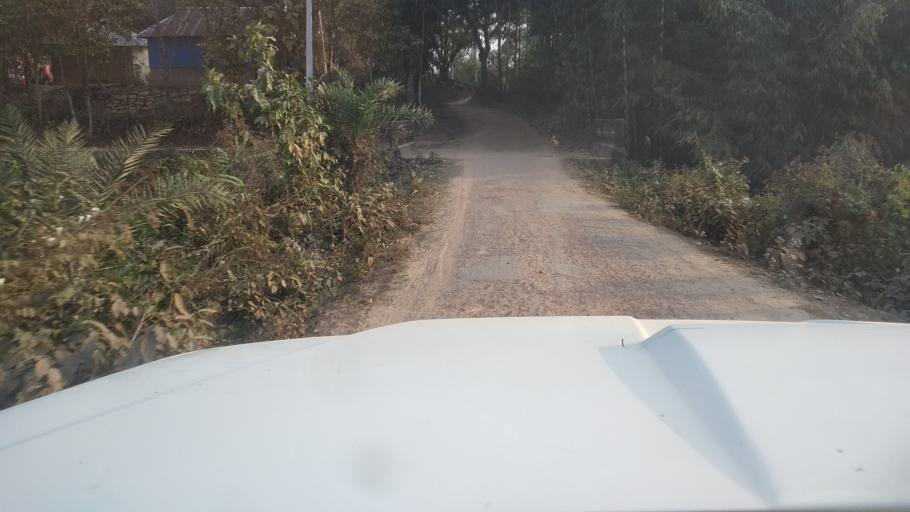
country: IN
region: Tripura
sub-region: West Tripura
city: Sonamura
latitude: 23.3260
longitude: 91.3025
